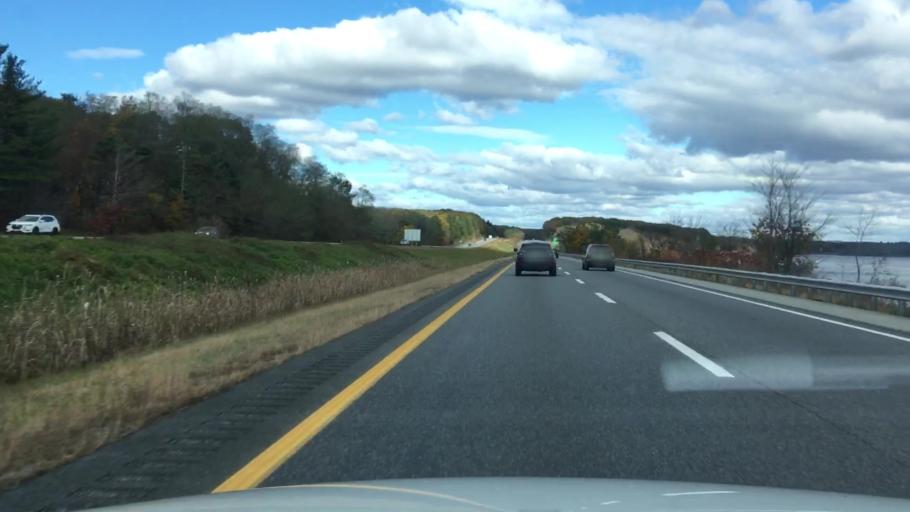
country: US
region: Maine
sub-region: Cumberland County
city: Portland
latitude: 43.6959
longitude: -70.2564
